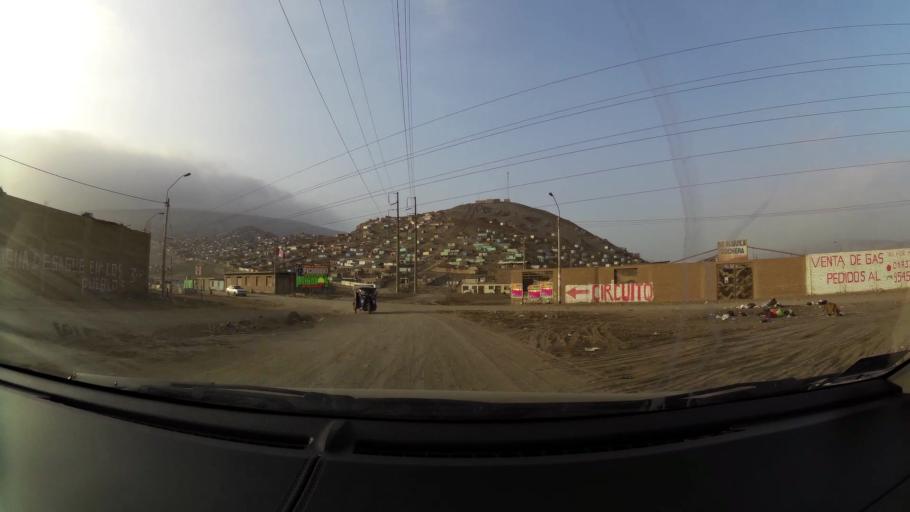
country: PE
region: Lima
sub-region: Lima
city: Santa Rosa
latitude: -11.7457
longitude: -77.1510
